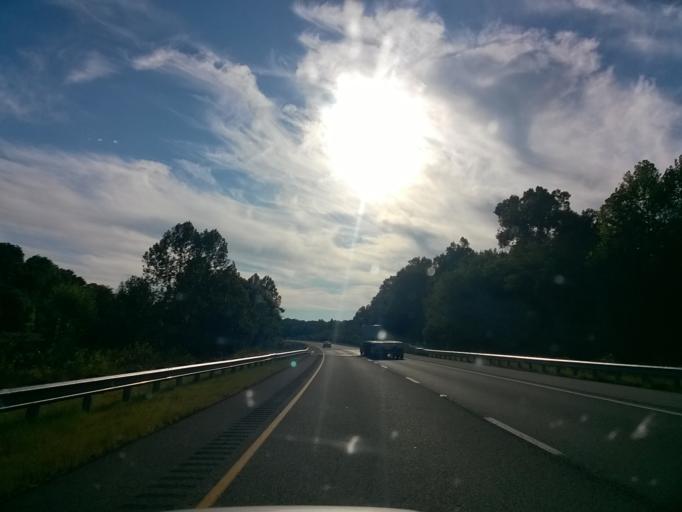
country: US
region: Indiana
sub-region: Spencer County
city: Dale
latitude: 38.1963
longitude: -87.1367
